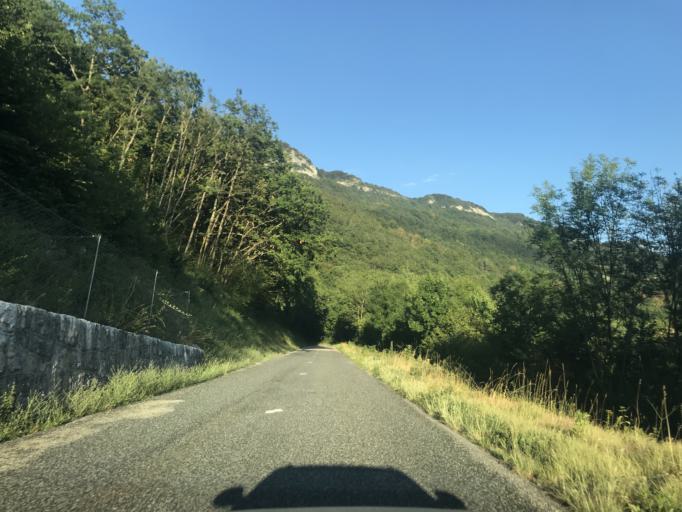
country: FR
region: Rhone-Alpes
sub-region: Departement de la Savoie
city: Brison-Saint-Innocent
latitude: 45.7150
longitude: 5.8239
